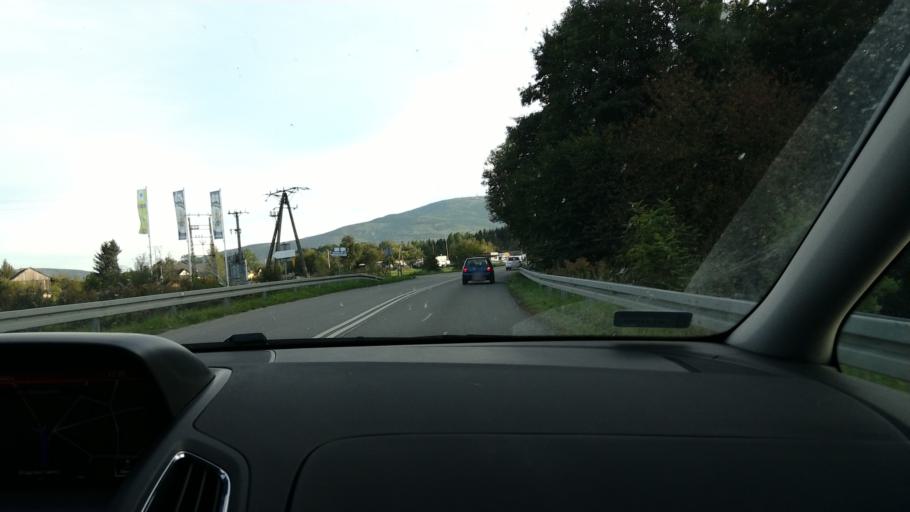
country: PL
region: Lower Silesian Voivodeship
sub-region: Powiat jeleniogorski
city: Myslakowice
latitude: 50.8258
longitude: 15.7779
